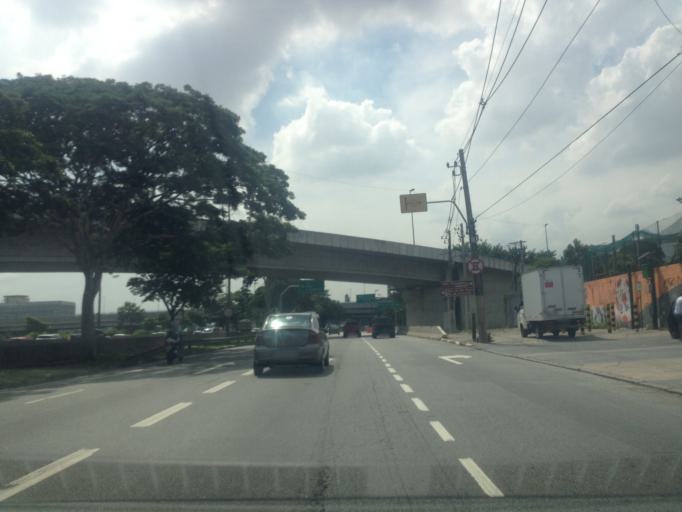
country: BR
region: Sao Paulo
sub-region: Sao Paulo
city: Sao Paulo
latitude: -23.5199
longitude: -46.6278
